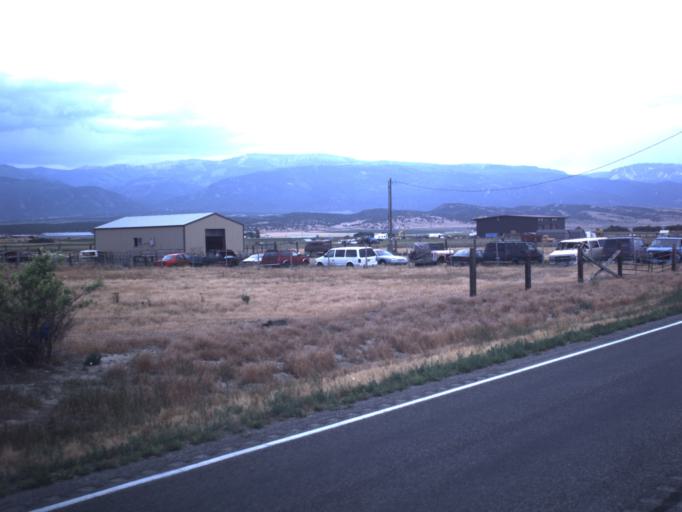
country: US
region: Utah
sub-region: Sanpete County
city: Moroni
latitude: 39.4883
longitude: -111.5631
